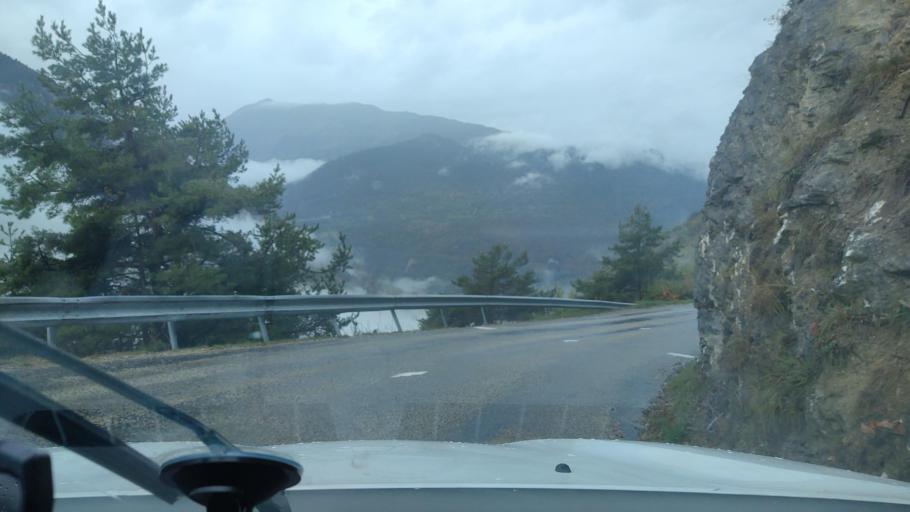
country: FR
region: Rhone-Alpes
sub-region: Departement de la Savoie
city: Les Allues
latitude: 45.4595
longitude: 6.5661
